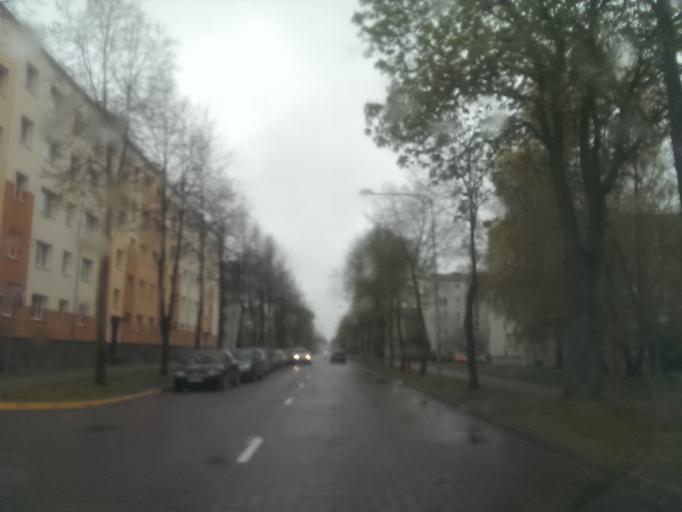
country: LV
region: Ventspils
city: Ventspils
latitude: 57.3911
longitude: 21.5724
